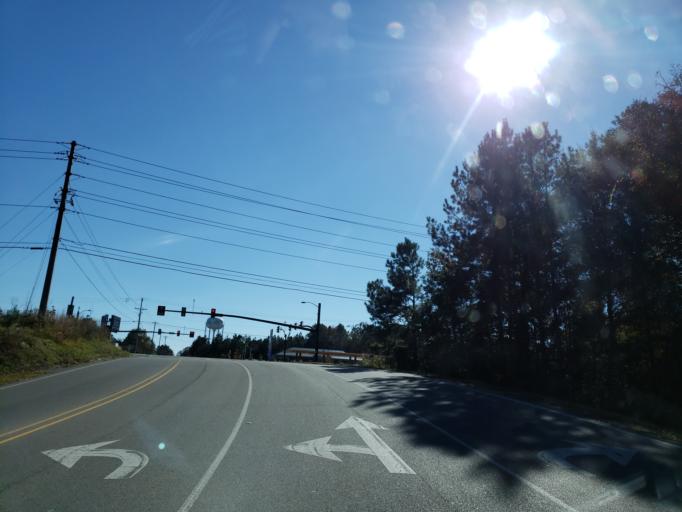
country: US
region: Mississippi
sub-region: Lamar County
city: West Hattiesburg
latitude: 31.3198
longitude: -89.3995
